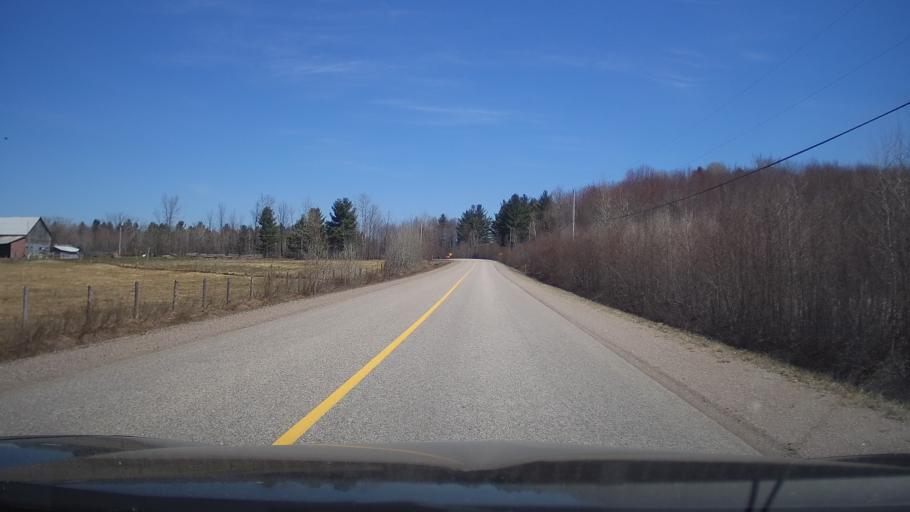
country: CA
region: Ontario
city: Arnprior
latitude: 45.5409
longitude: -76.3666
